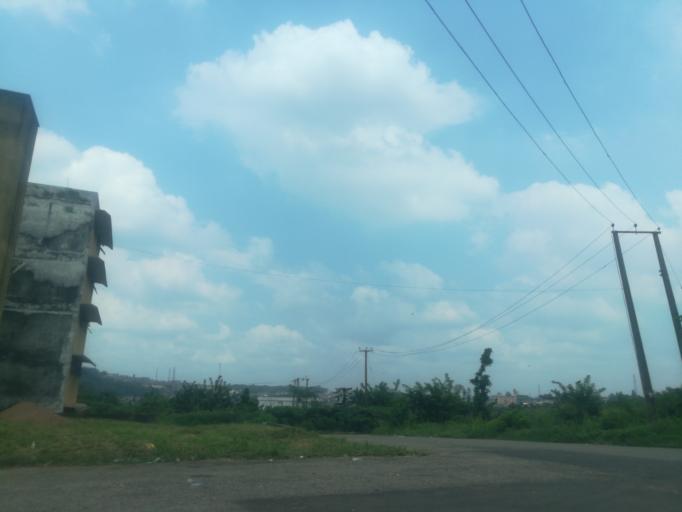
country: NG
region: Oyo
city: Ibadan
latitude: 7.4118
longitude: 3.9055
